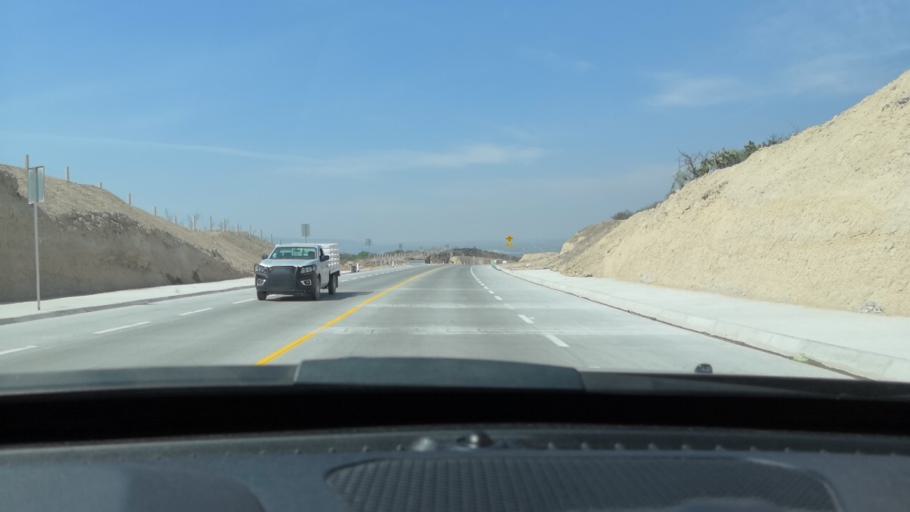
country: MX
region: Guanajuato
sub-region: San Francisco del Rincon
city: Estacion de San Francisco
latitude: 21.0879
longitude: -101.7976
